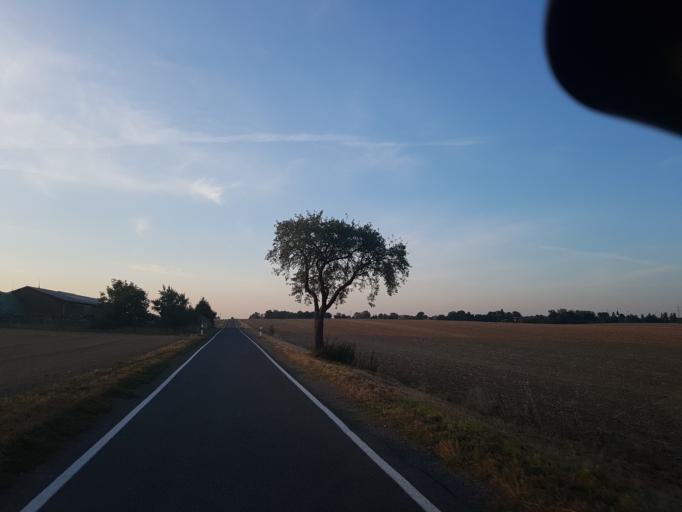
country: DE
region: Saxony
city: Stauchitz
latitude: 51.2988
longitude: 13.1894
